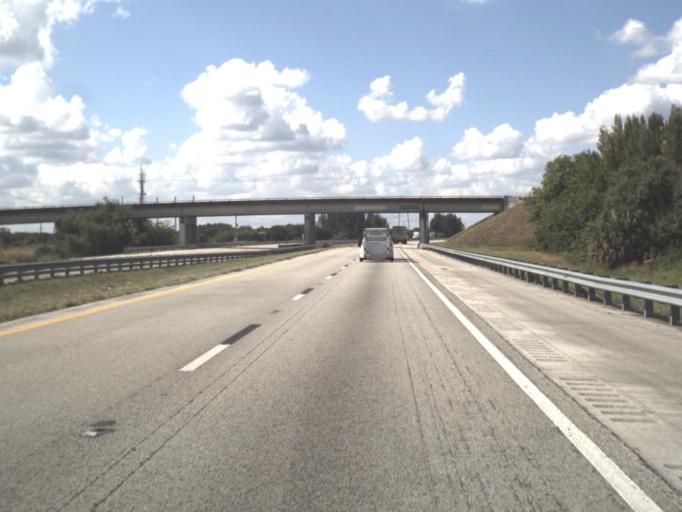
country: US
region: Florida
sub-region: Saint Lucie County
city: Lakewood Park
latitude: 27.4853
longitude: -80.5577
